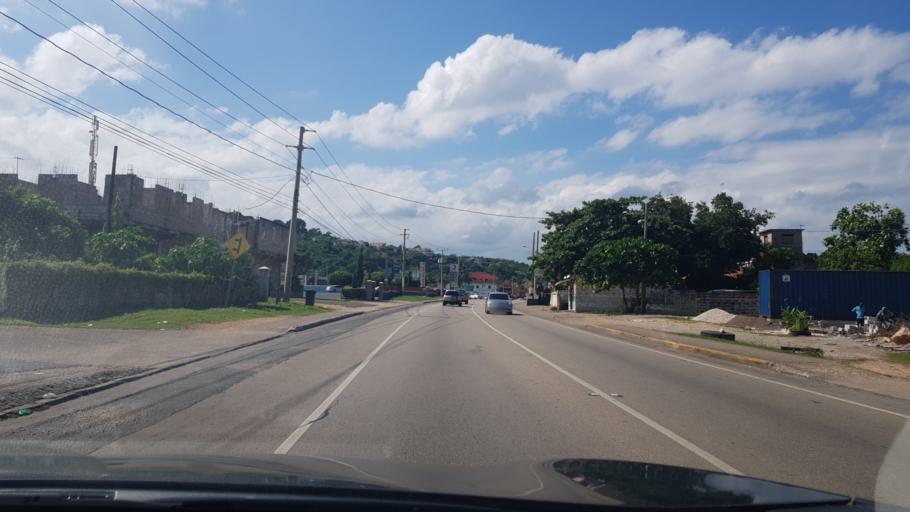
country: JM
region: Saint Ann
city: Discovery Bay
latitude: 18.4615
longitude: -77.3967
